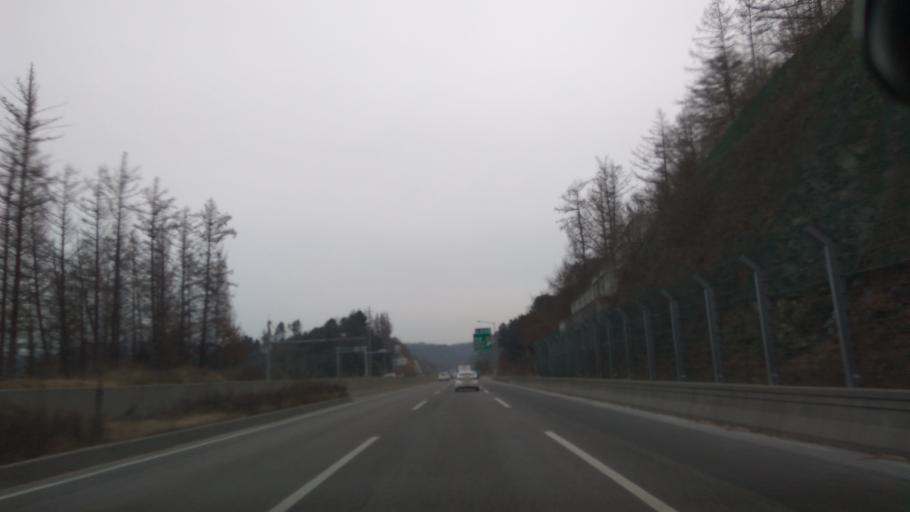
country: KR
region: Gangwon-do
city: Sindong
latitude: 37.7320
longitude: 127.6182
